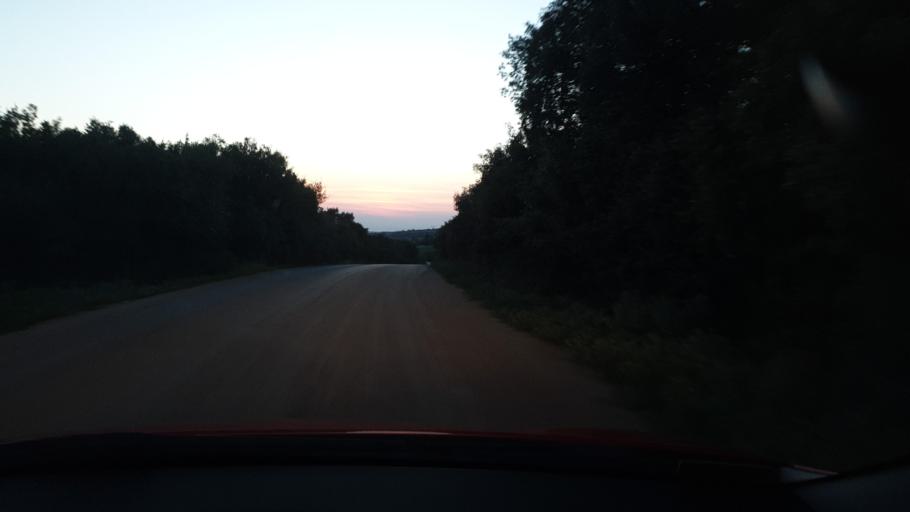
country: GR
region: Central Macedonia
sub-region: Nomos Thessalonikis
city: Vasilika
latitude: 40.5084
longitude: 23.1442
